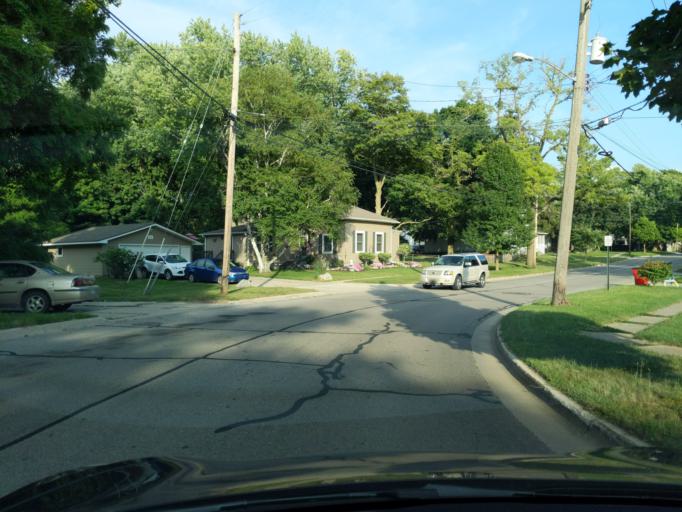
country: US
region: Michigan
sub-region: Eaton County
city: Grand Ledge
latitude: 42.7590
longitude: -84.7455
